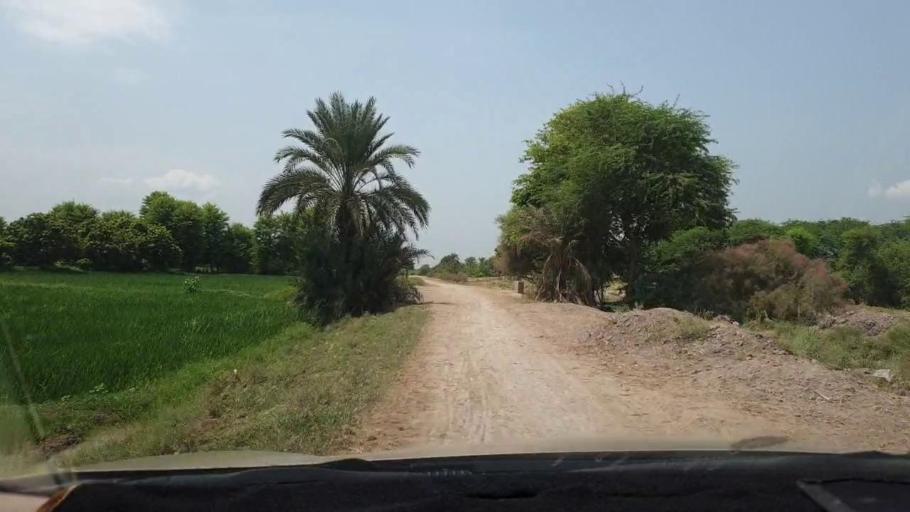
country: PK
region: Sindh
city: Naudero
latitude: 27.6629
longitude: 68.3032
